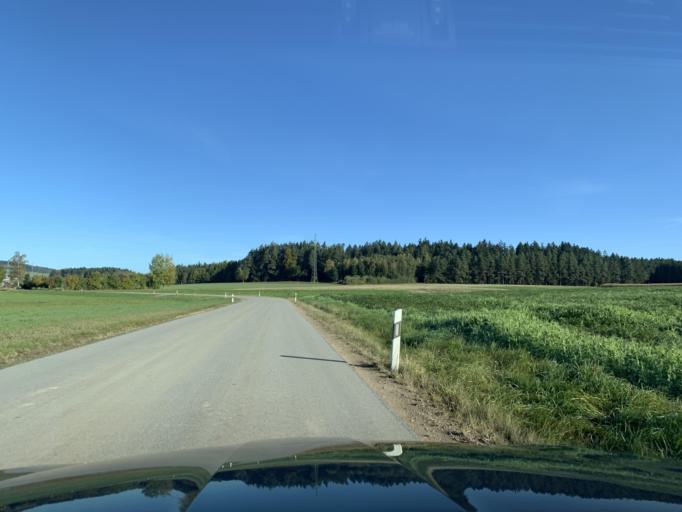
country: DE
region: Bavaria
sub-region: Upper Palatinate
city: Thanstein
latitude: 49.3895
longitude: 12.4780
